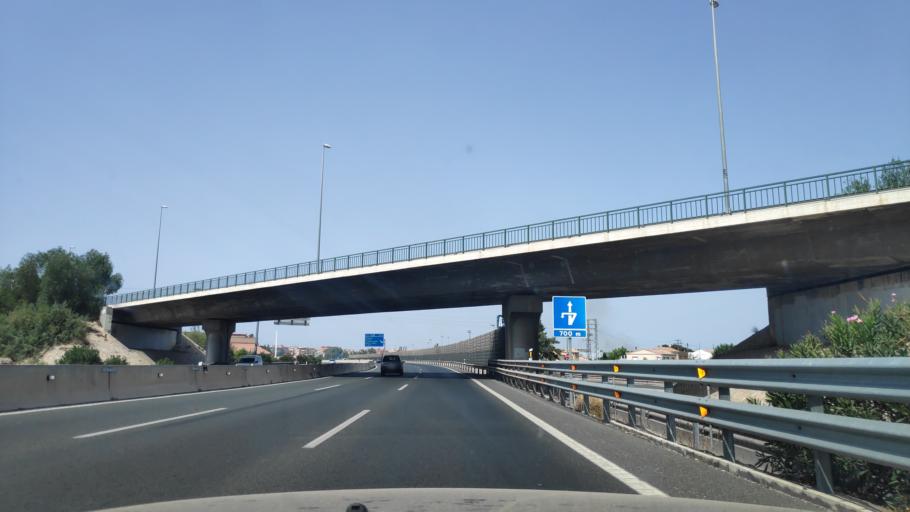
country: ES
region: Murcia
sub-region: Murcia
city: Murcia
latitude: 37.9574
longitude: -1.1365
